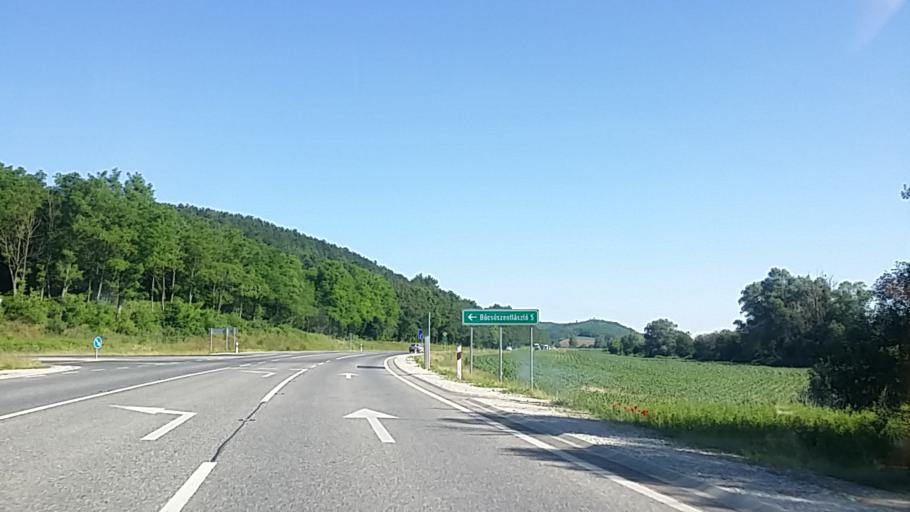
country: HU
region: Zala
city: Zalaegerszeg
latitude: 46.8289
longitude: 16.9302
